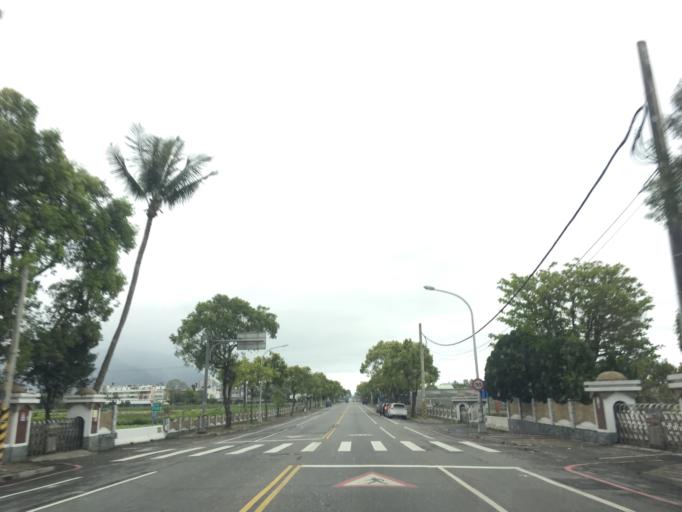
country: TW
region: Taiwan
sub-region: Hualien
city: Hualian
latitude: 23.9746
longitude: 121.5640
